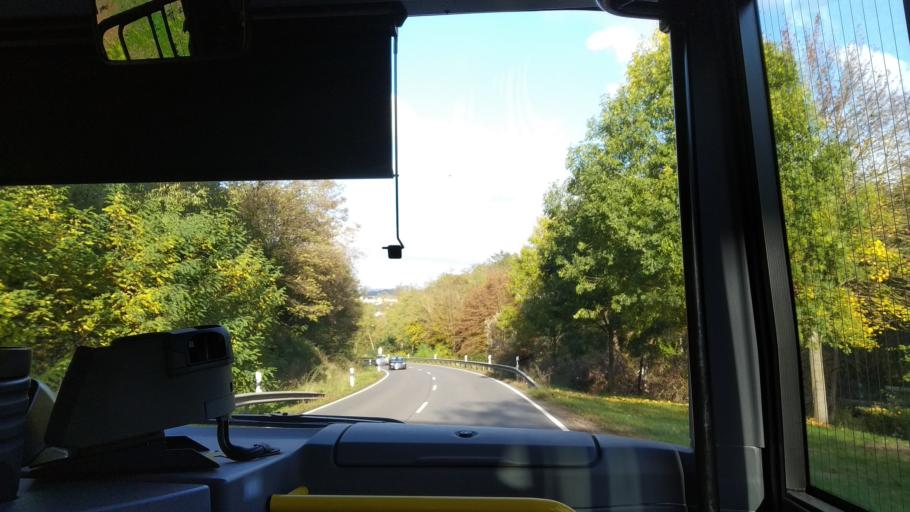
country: DE
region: Rheinland-Pfalz
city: Diez
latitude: 50.3622
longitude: 8.0221
